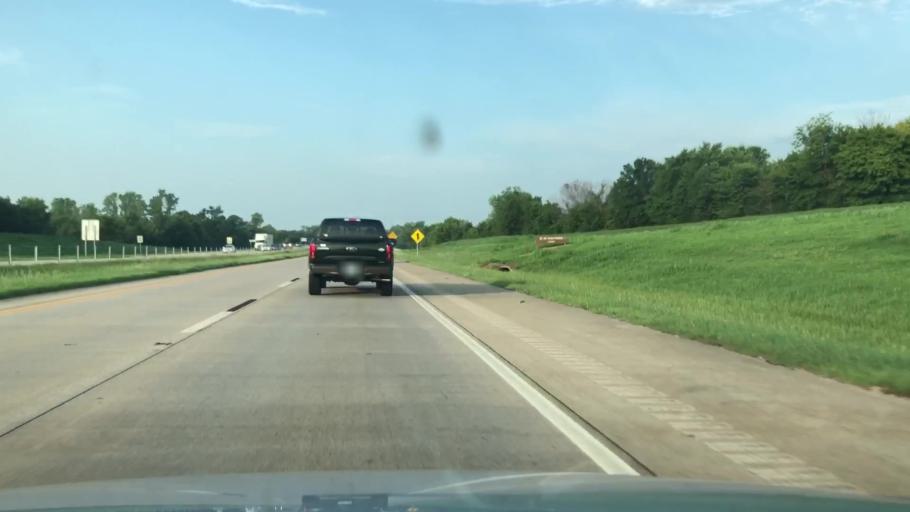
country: US
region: Oklahoma
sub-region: Tulsa County
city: Turley
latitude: 36.2486
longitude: -95.9337
